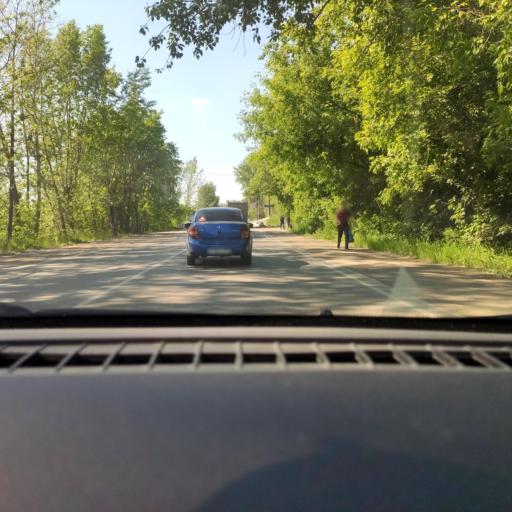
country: RU
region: Perm
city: Krasnokamsk
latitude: 58.0679
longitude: 55.7942
